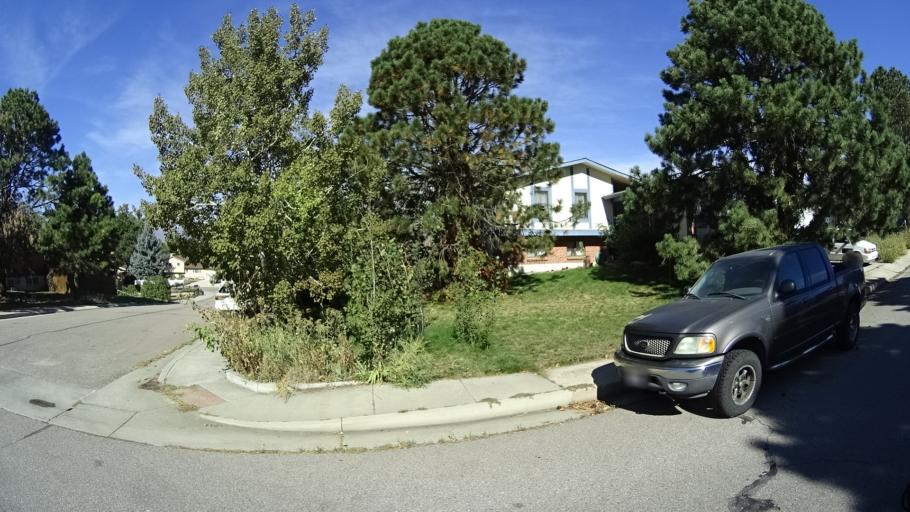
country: US
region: Colorado
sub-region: El Paso County
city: Cimarron Hills
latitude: 38.9168
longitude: -104.7684
